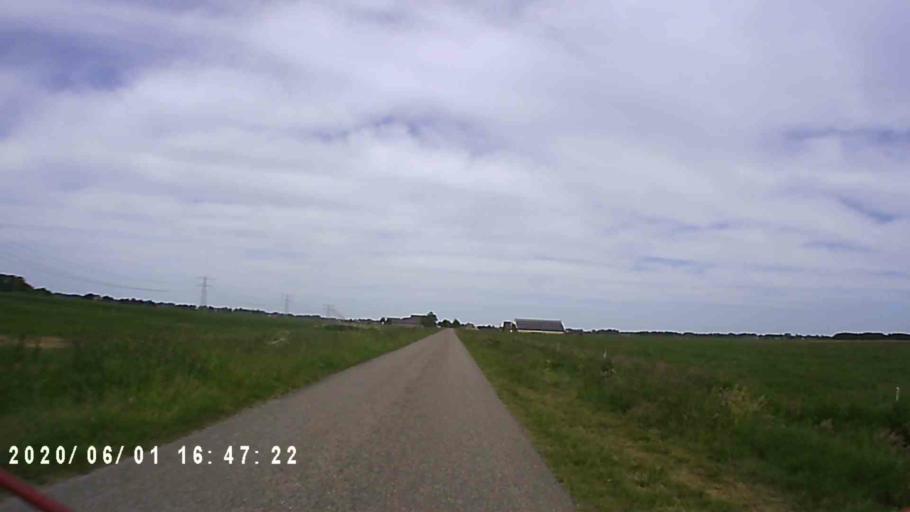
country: NL
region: Friesland
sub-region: Gemeente Tytsjerksteradiel
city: Tytsjerk
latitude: 53.1865
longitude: 5.8960
